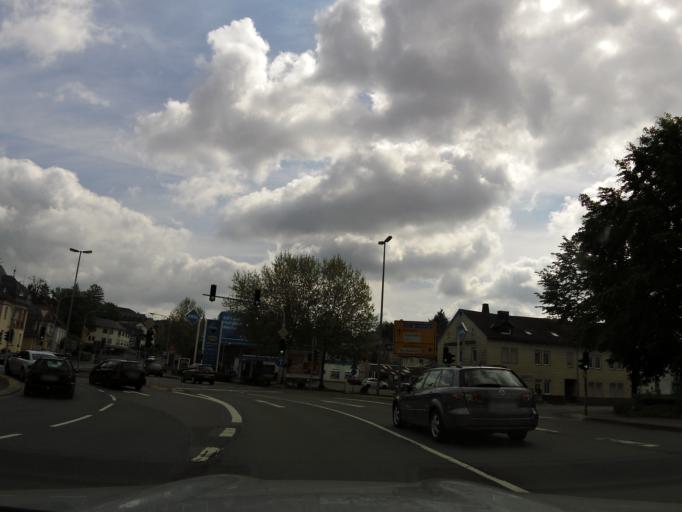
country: DE
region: Hesse
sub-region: Regierungsbezirk Giessen
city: Wetzlar
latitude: 50.5508
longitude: 8.5014
